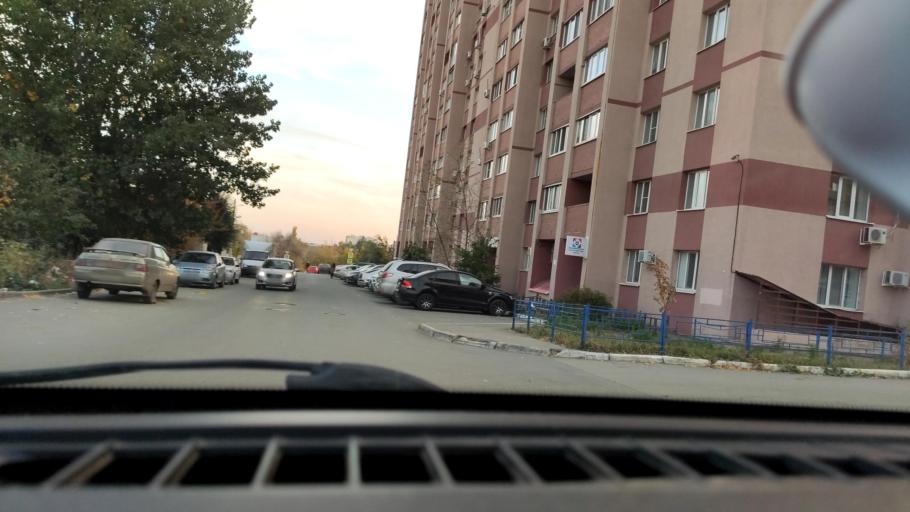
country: RU
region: Samara
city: Samara
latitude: 53.2076
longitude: 50.2083
